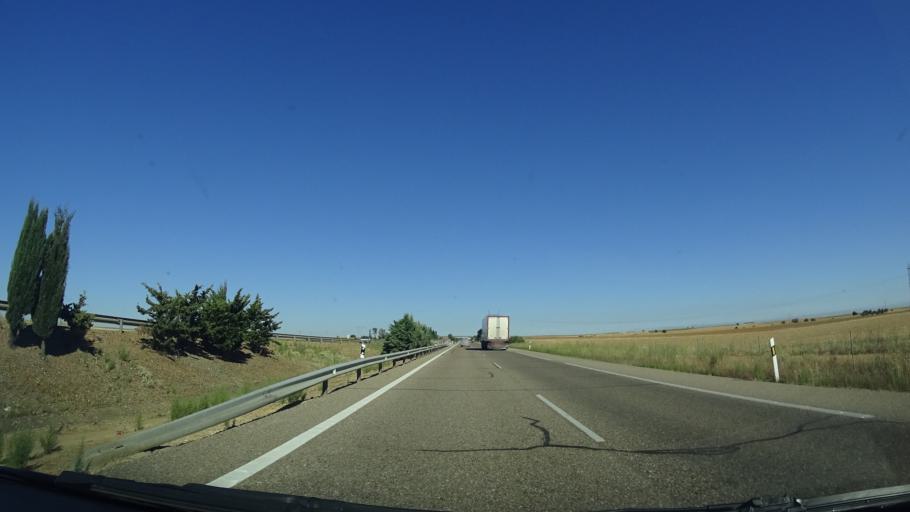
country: ES
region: Castille and Leon
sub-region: Provincia de Zamora
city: Cerecinos de Campos
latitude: 41.9147
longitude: -5.5099
